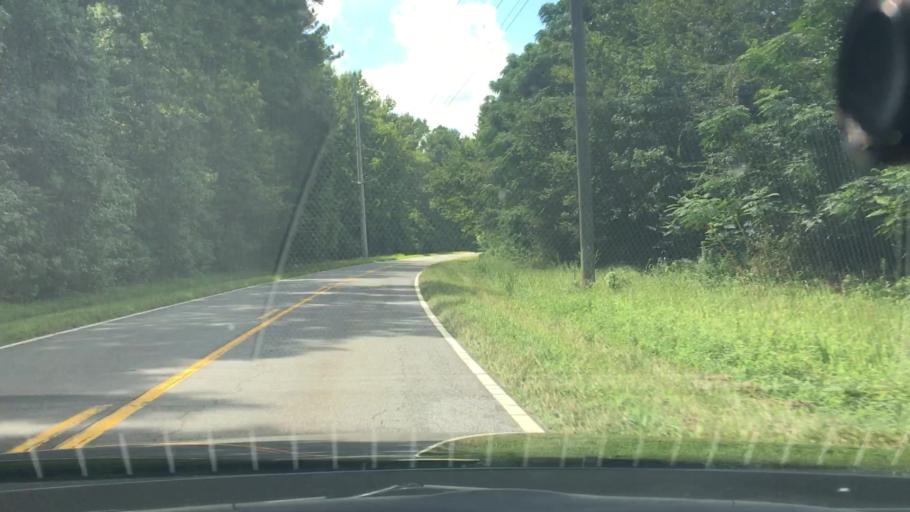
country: US
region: Georgia
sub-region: Putnam County
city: Jefferson
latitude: 33.3670
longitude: -83.2837
